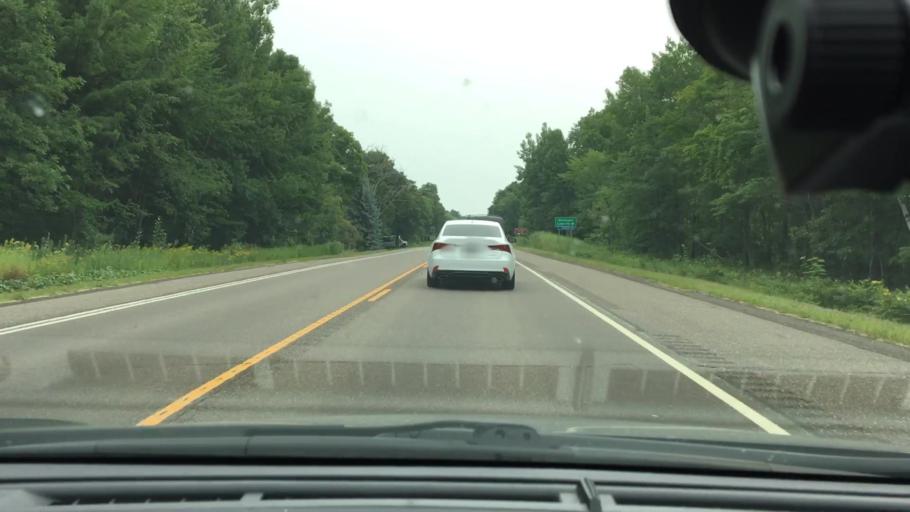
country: US
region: Minnesota
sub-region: Mille Lacs County
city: Vineland
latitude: 46.1469
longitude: -93.7294
